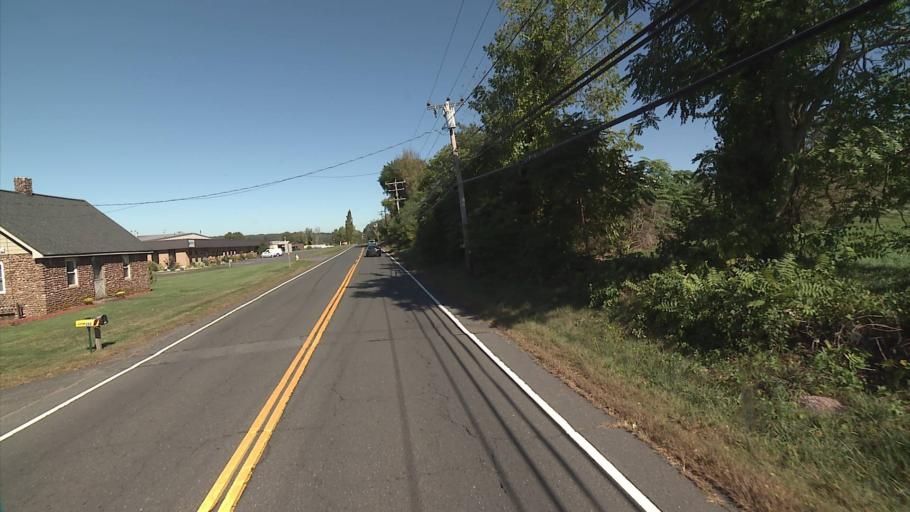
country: US
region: Connecticut
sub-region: Tolland County
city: Ellington
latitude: 41.9243
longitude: -72.4540
